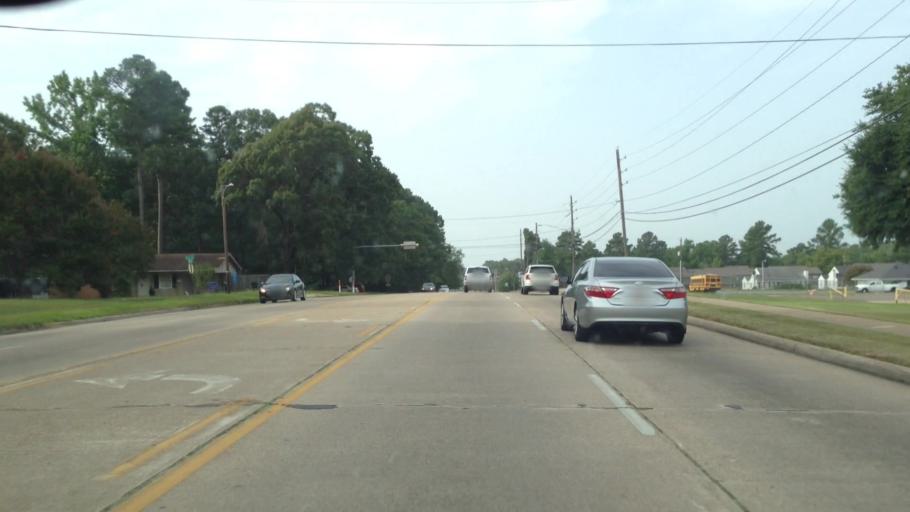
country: US
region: Louisiana
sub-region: De Soto Parish
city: Stonewall
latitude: 32.4079
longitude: -93.8147
